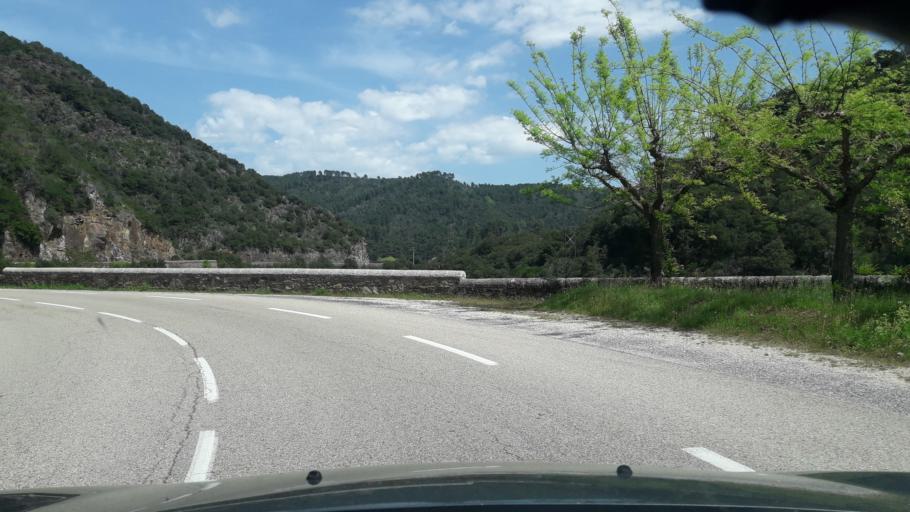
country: FR
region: Languedoc-Roussillon
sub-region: Departement du Gard
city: Lasalle
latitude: 44.1027
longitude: 3.8059
